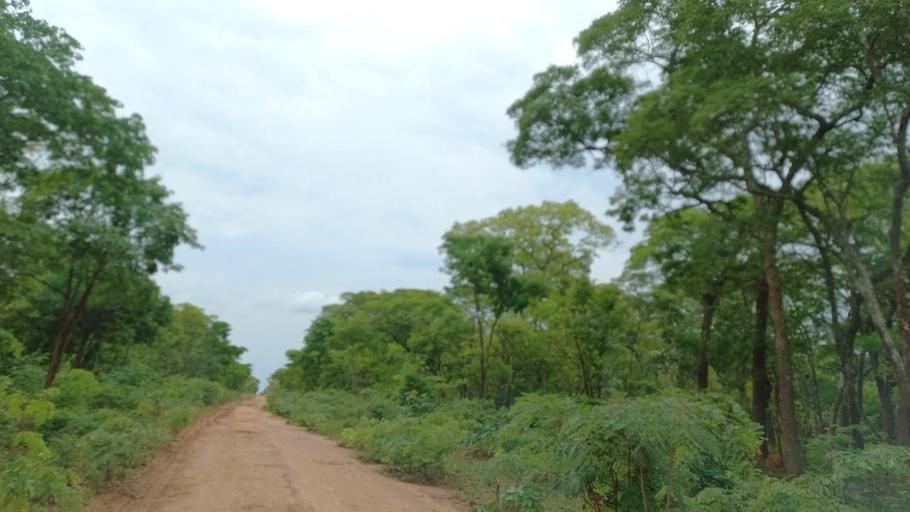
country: ZM
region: North-Western
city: Kalengwa
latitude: -13.6062
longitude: 24.9750
